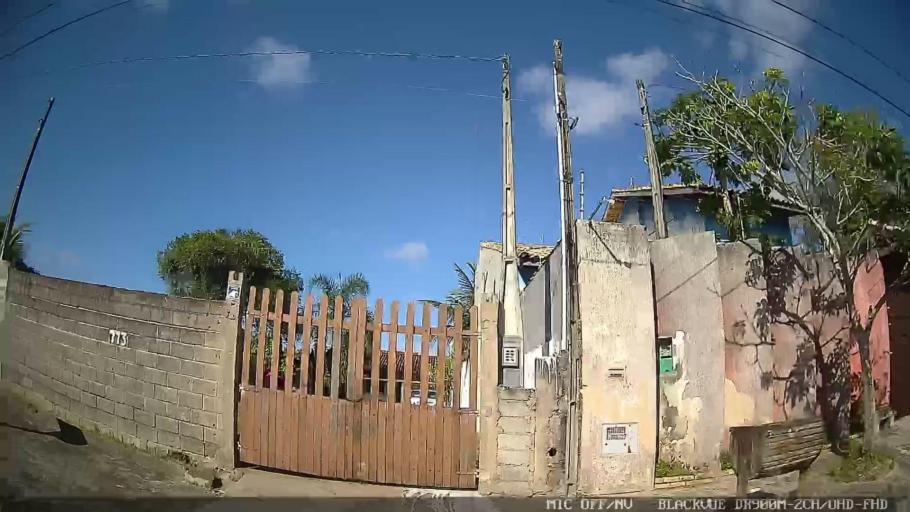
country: BR
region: Sao Paulo
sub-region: Peruibe
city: Peruibe
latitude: -24.2696
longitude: -46.9397
